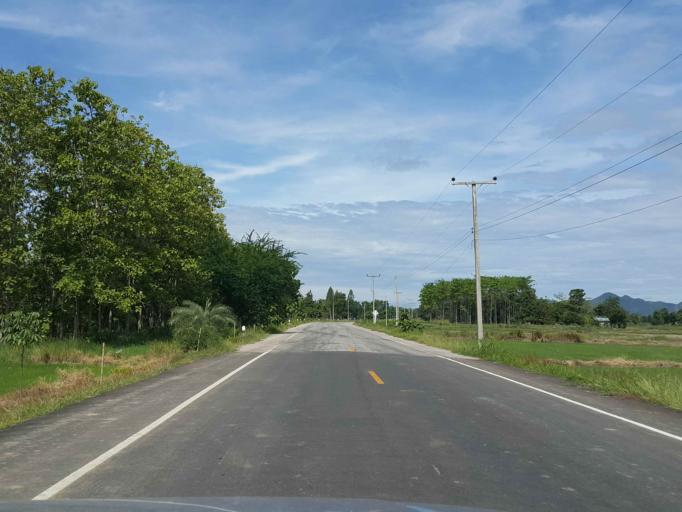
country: TH
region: Sukhothai
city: Ban Dan Lan Hoi
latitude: 17.1151
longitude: 99.5268
